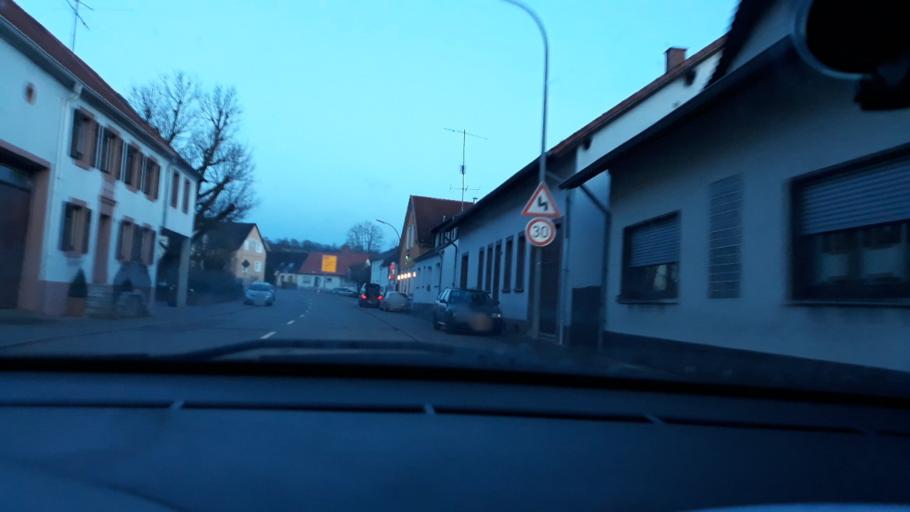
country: FR
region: Lorraine
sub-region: Departement de la Moselle
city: Sarreguemines
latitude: 49.1535
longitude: 7.1113
